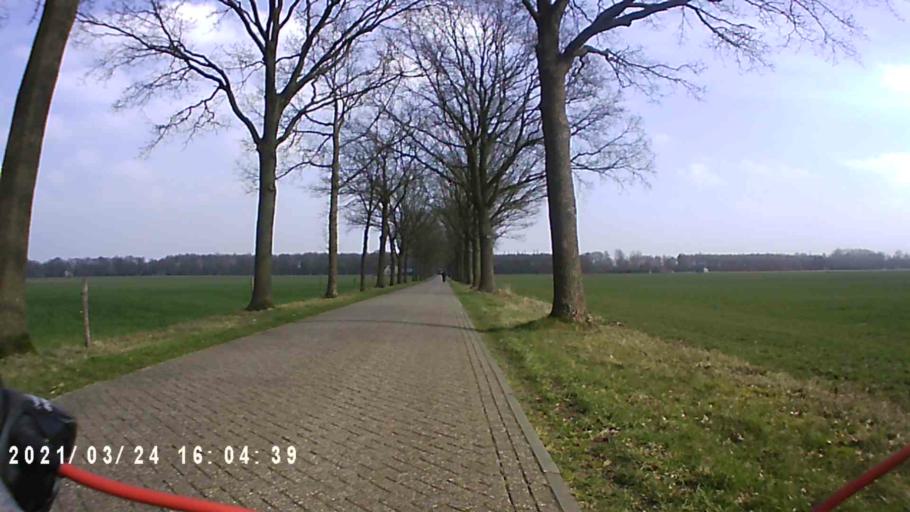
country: NL
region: Friesland
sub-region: Gemeente Heerenveen
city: Jubbega
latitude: 53.0319
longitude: 6.2106
